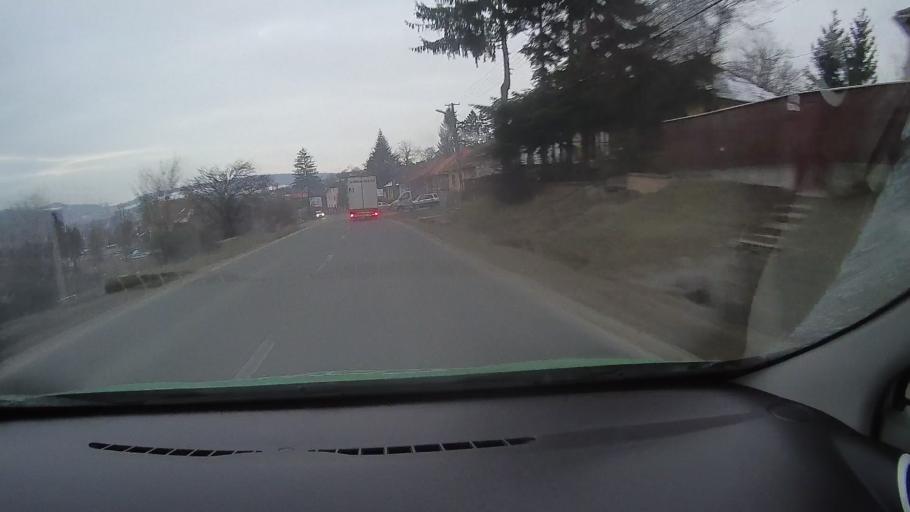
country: RO
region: Harghita
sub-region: Municipiul Odorheiu Secuiesc
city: Odorheiu Secuiesc
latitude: 46.3177
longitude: 25.2806
